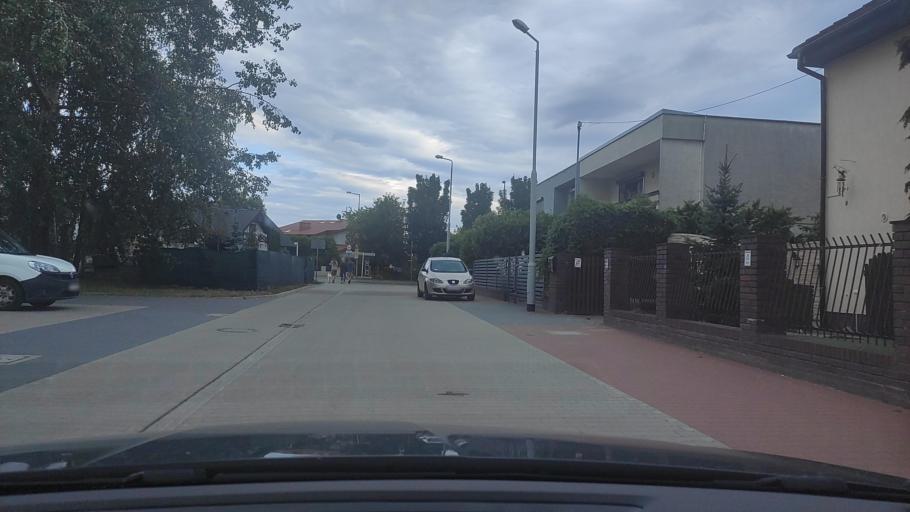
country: PL
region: Greater Poland Voivodeship
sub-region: Powiat poznanski
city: Swarzedz
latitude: 52.3960
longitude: 17.0616
